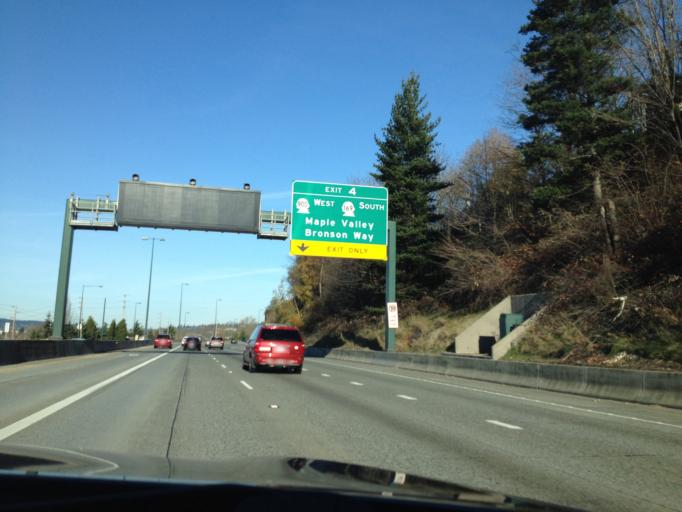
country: US
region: Washington
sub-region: King County
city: Renton
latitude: 47.4753
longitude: -122.2036
